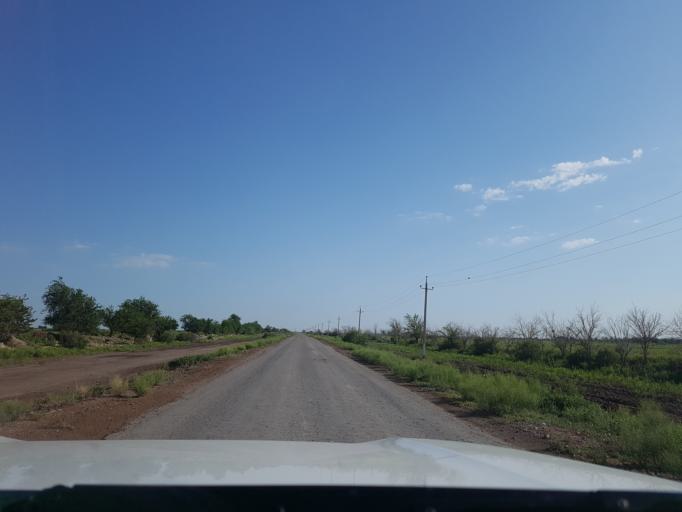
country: TM
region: Dasoguz
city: Koeneuergench
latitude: 41.8515
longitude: 58.7049
